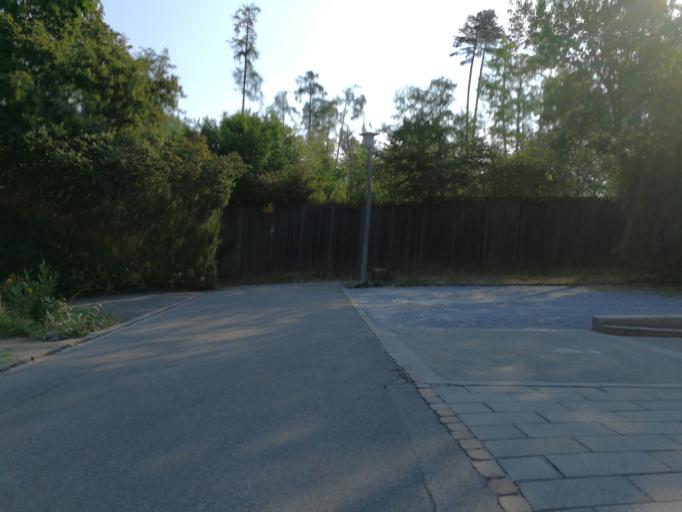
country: CH
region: Zurich
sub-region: Bezirk Uster
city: Egg
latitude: 47.3031
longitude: 8.6945
